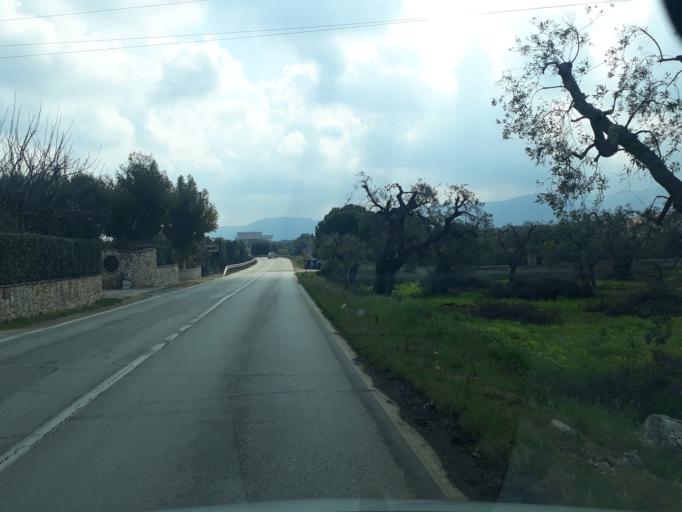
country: IT
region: Apulia
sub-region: Provincia di Brindisi
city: Fasano
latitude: 40.8249
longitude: 17.3709
